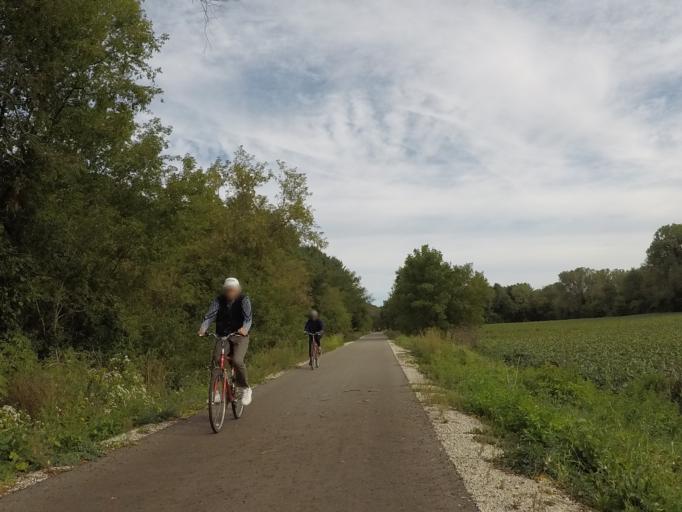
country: US
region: Wisconsin
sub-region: Sauk County
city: Prairie du Sac
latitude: 43.3548
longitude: -89.7405
